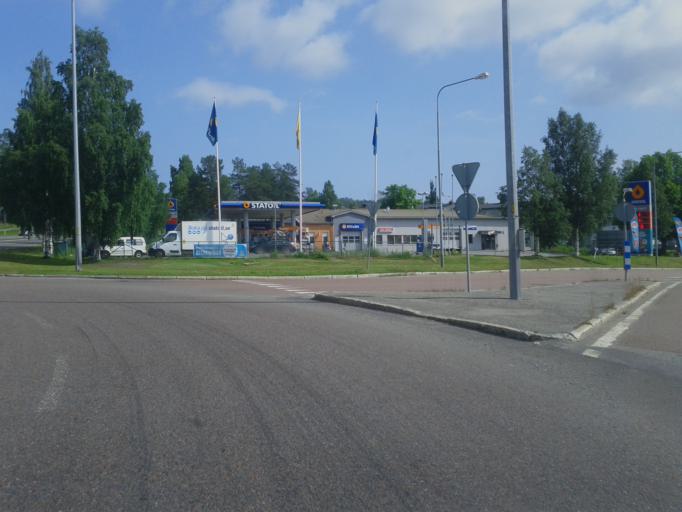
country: SE
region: Vaesterbotten
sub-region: Skelleftea Kommun
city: Skelleftea
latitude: 64.7577
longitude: 20.9651
